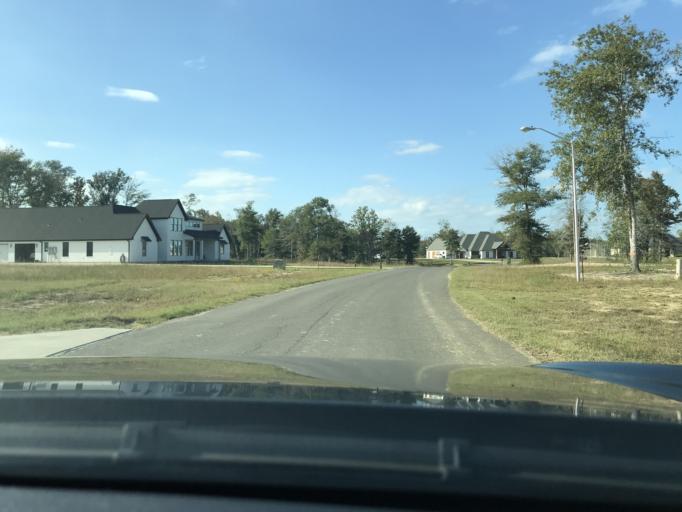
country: US
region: Louisiana
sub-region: Calcasieu Parish
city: Moss Bluff
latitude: 30.3329
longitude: -93.2508
